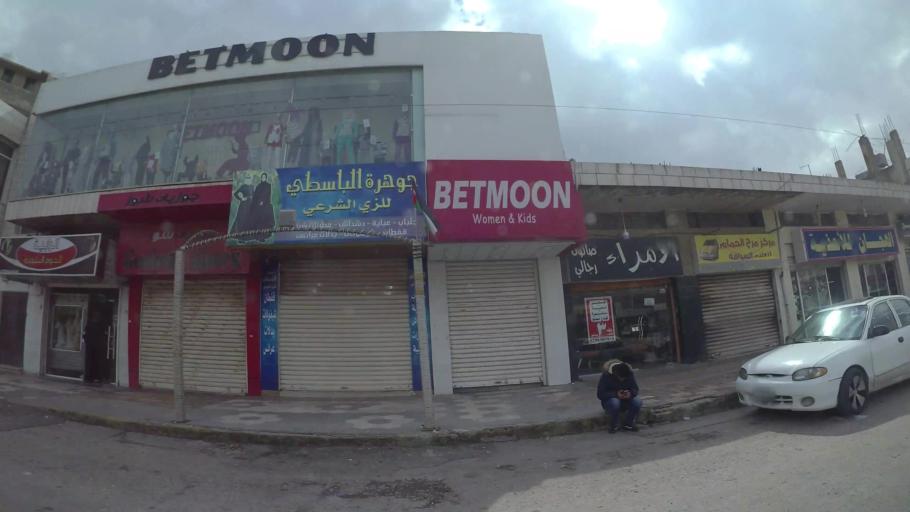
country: JO
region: Amman
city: Umm as Summaq
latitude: 31.8966
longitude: 35.8402
